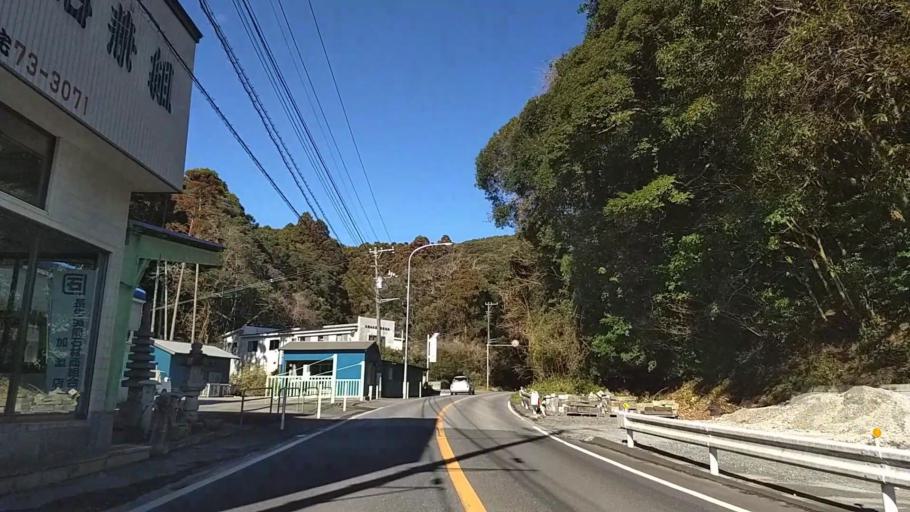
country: JP
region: Chiba
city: Katsuura
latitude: 35.1605
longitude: 140.3271
